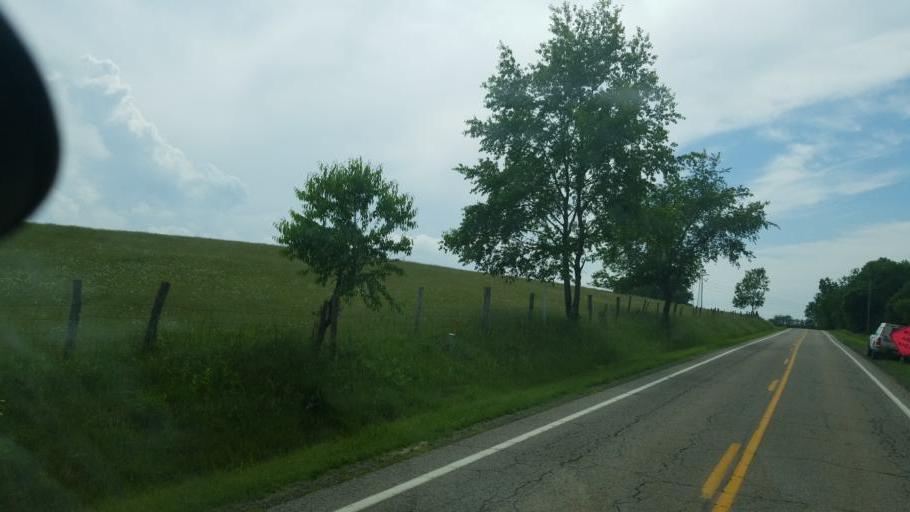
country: US
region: Ohio
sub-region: Knox County
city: Oak Hill
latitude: 40.2893
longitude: -82.2173
